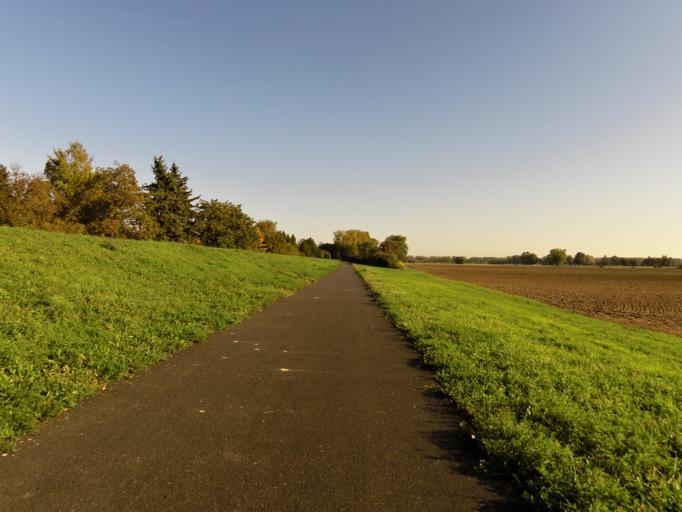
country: DE
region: Rheinland-Pfalz
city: Eich
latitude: 49.7629
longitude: 8.4302
